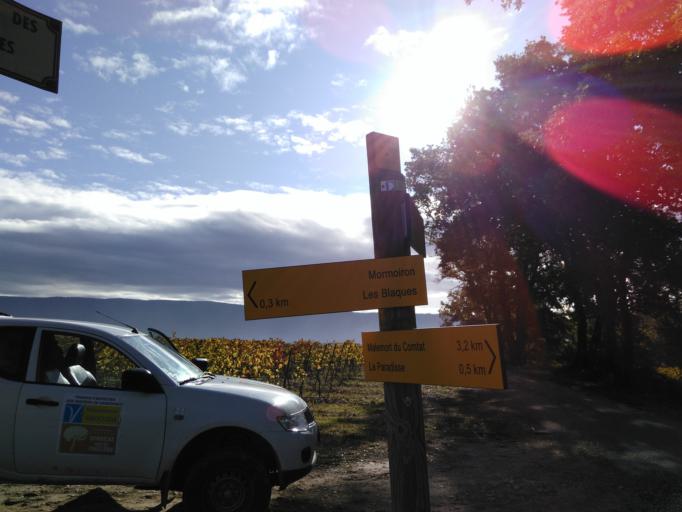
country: FR
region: Provence-Alpes-Cote d'Azur
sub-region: Departement du Vaucluse
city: Malemort-du-Comtat
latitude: 44.0281
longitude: 5.1855
